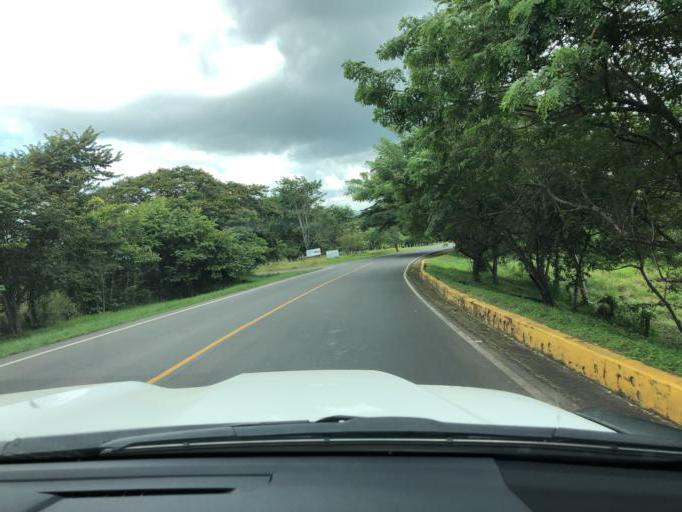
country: NI
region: Chontales
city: Santo Tomas
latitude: 12.0614
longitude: -85.0567
